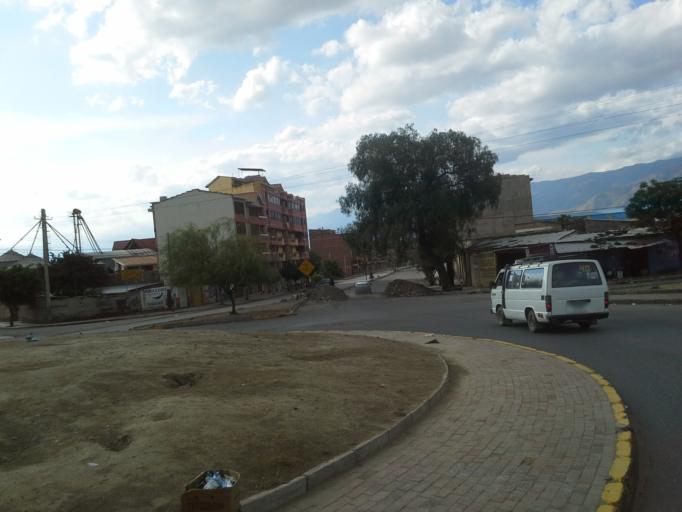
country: BO
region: Cochabamba
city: Cochabamba
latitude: -17.4170
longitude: -66.1517
